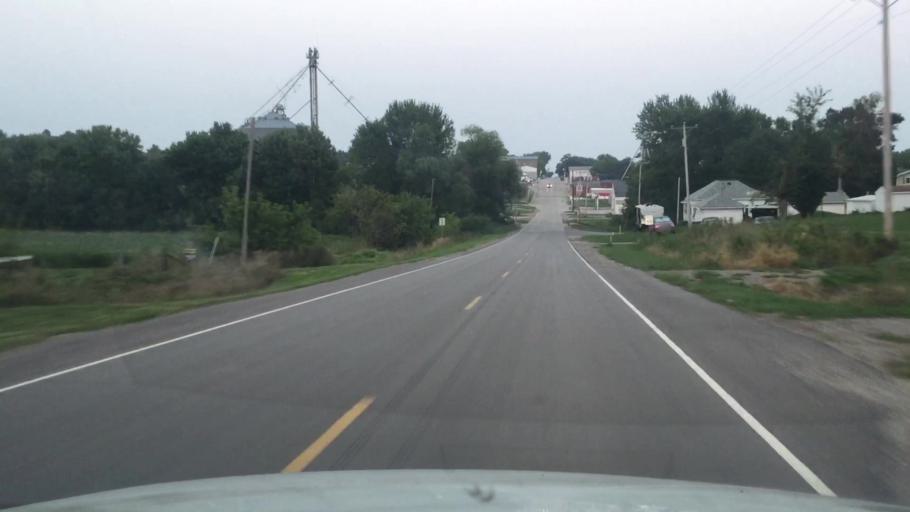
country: US
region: Iowa
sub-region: Marion County
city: Melcher-Dallas
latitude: 41.1895
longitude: -93.3908
